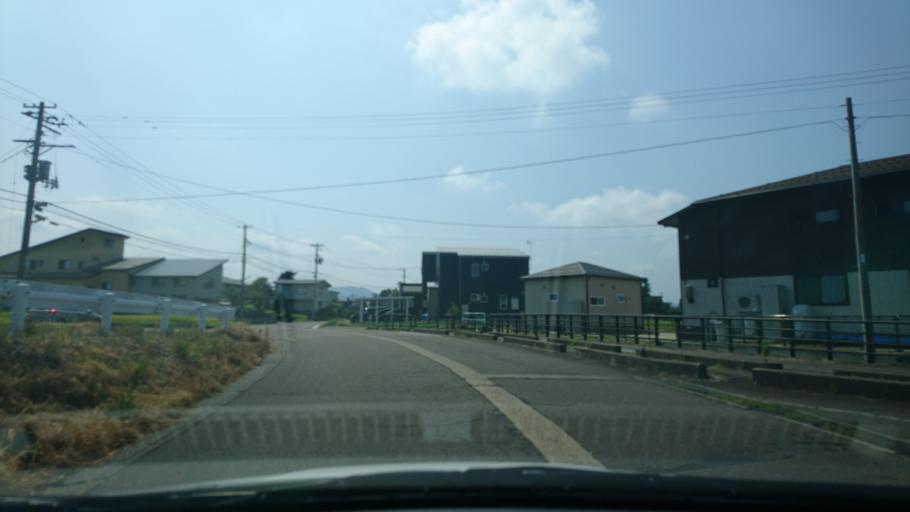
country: JP
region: Niigata
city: Arai
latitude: 37.0553
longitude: 138.2548
